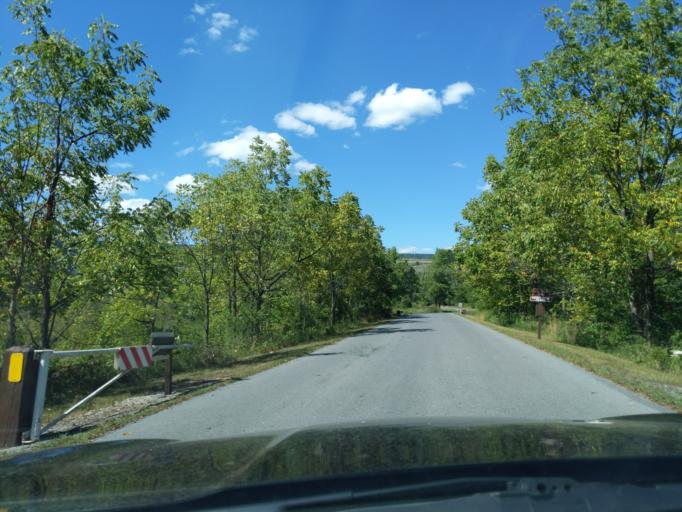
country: US
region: Pennsylvania
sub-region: Blair County
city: Greenwood
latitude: 40.4774
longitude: -78.2896
